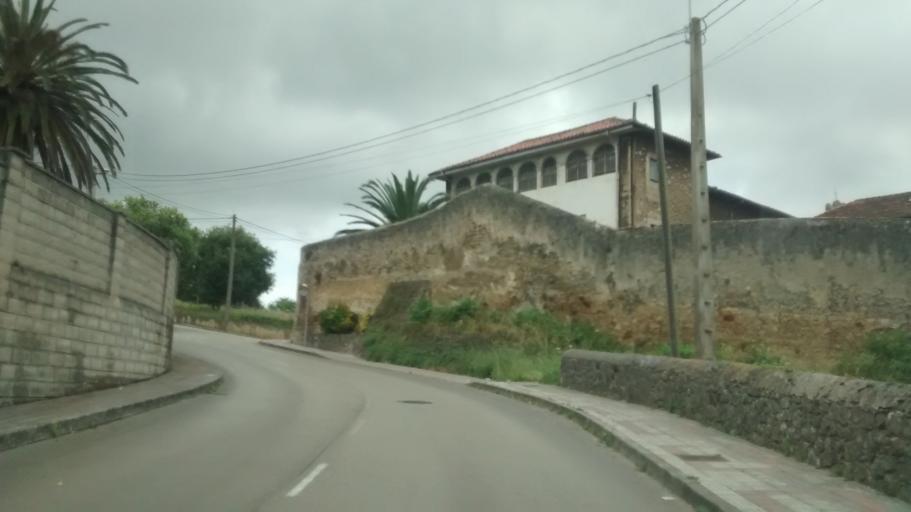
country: ES
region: Cantabria
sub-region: Provincia de Cantabria
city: El Astillero
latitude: 43.4191
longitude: -3.8292
